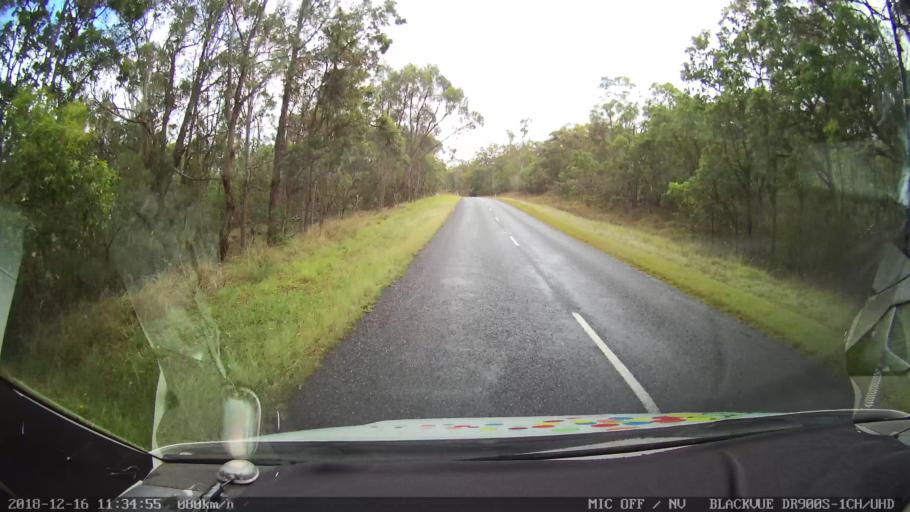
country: AU
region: New South Wales
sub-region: Tenterfield Municipality
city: Carrolls Creek
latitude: -28.9953
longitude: 152.1587
